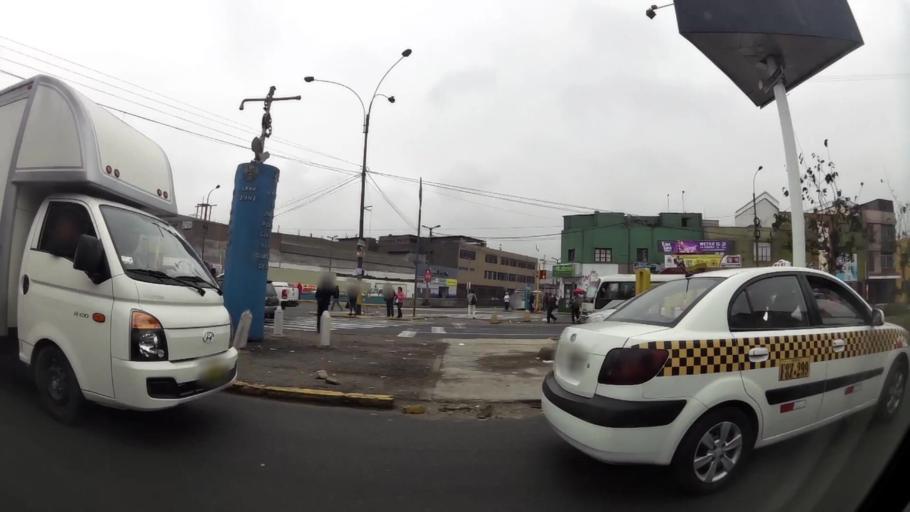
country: PE
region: Lima
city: Lima
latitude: -12.0558
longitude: -77.0573
